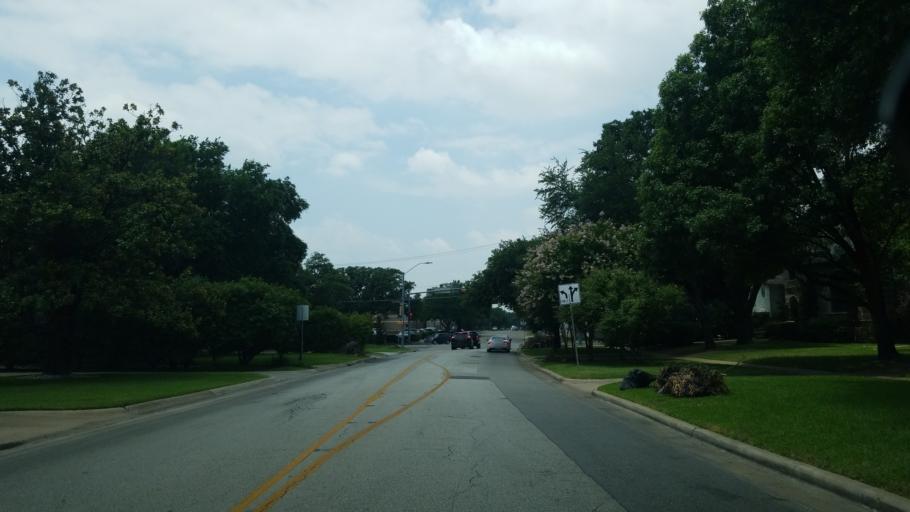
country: US
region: Texas
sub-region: Dallas County
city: University Park
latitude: 32.8450
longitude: -96.8203
